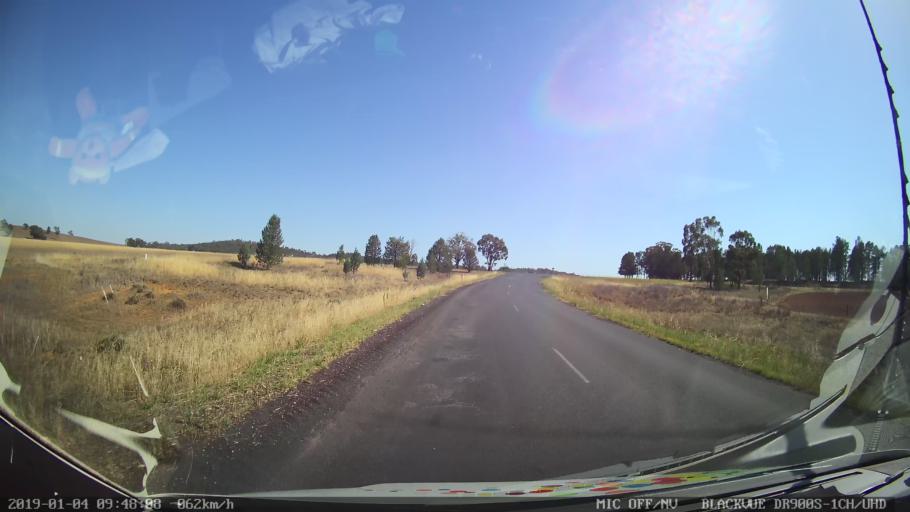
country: AU
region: New South Wales
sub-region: Cabonne
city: Canowindra
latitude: -33.5993
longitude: 148.4323
